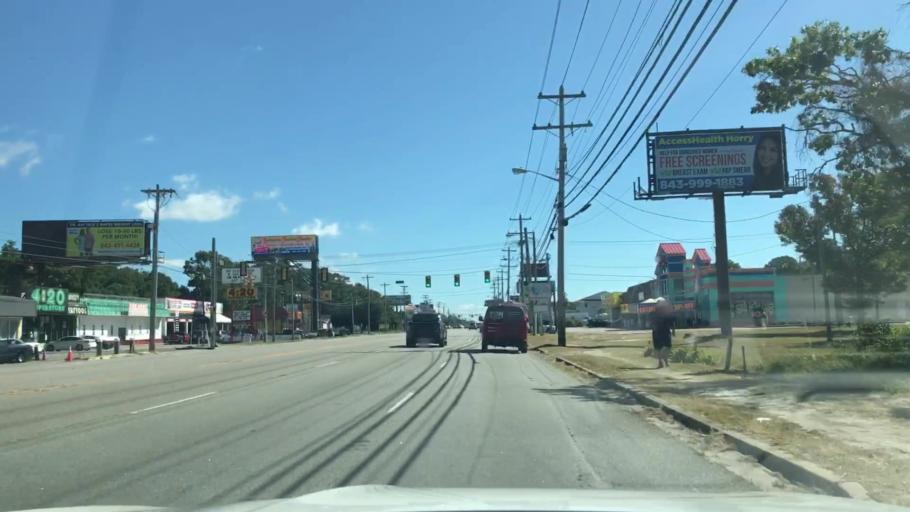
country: US
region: South Carolina
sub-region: Horry County
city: North Myrtle Beach
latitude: 33.8054
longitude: -78.7194
